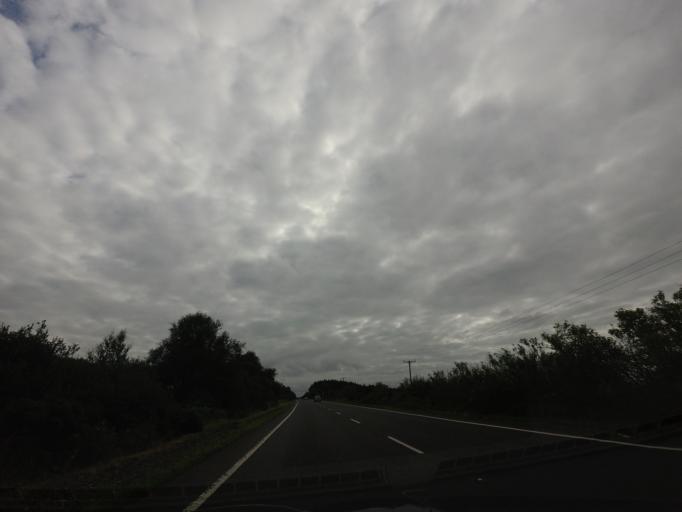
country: GB
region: Scotland
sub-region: Dumfries and Galloway
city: Gretna
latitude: 54.9919
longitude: -3.1576
